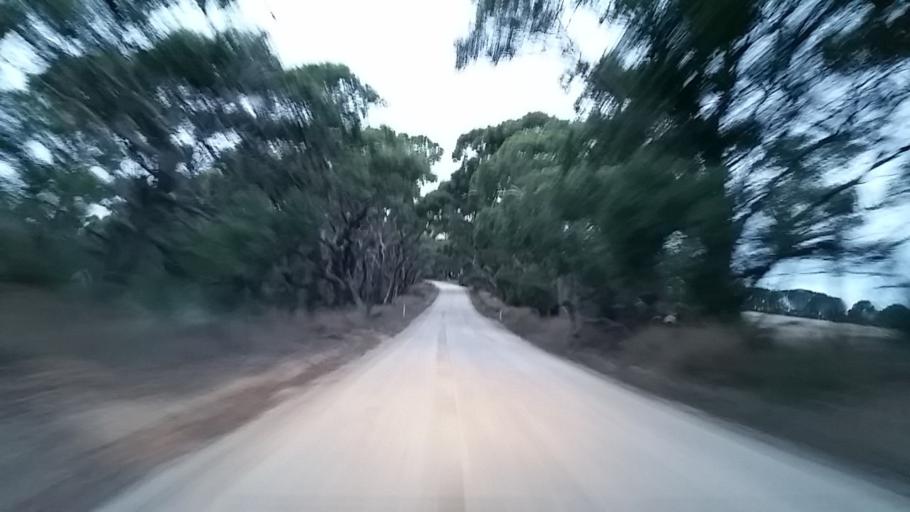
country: AU
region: South Australia
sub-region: Yankalilla
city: Normanville
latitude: -35.6108
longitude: 138.1716
